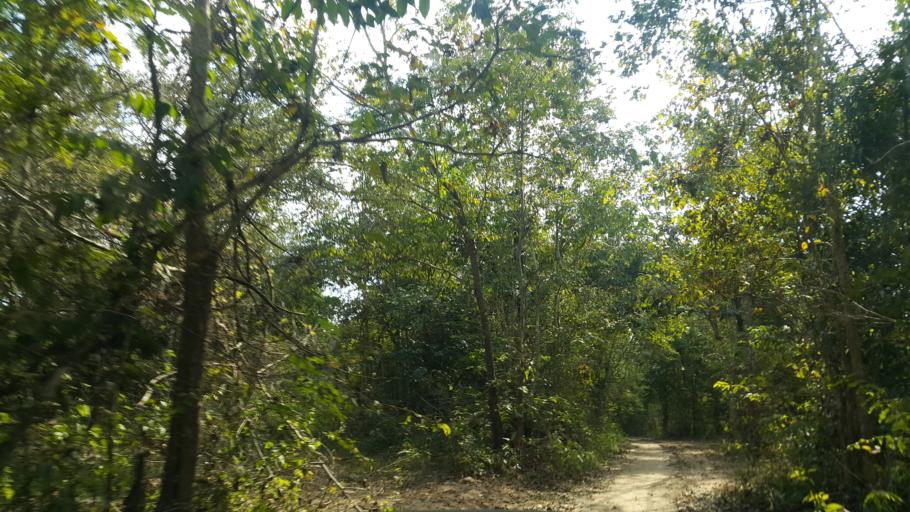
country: TH
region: Lamphun
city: Ban Thi
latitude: 18.5846
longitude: 99.1648
